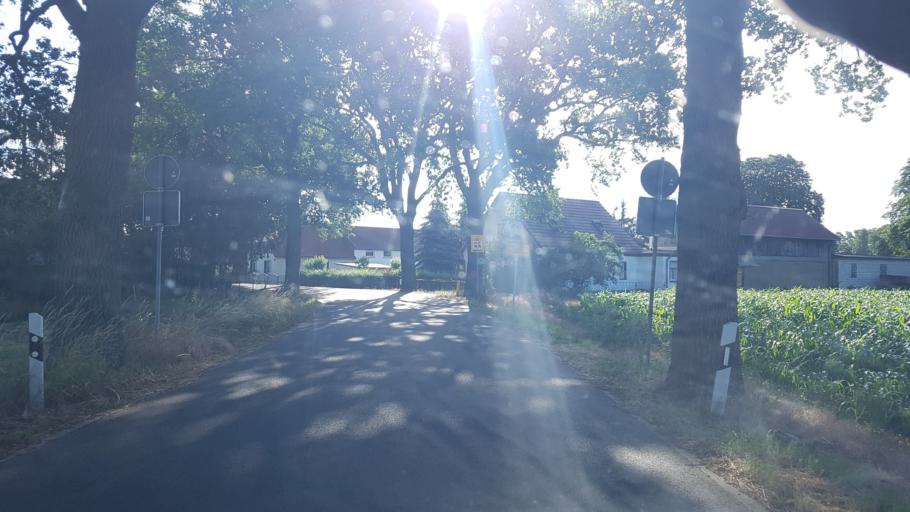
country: DE
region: Brandenburg
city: Kasel-Golzig
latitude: 51.9568
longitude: 13.6664
